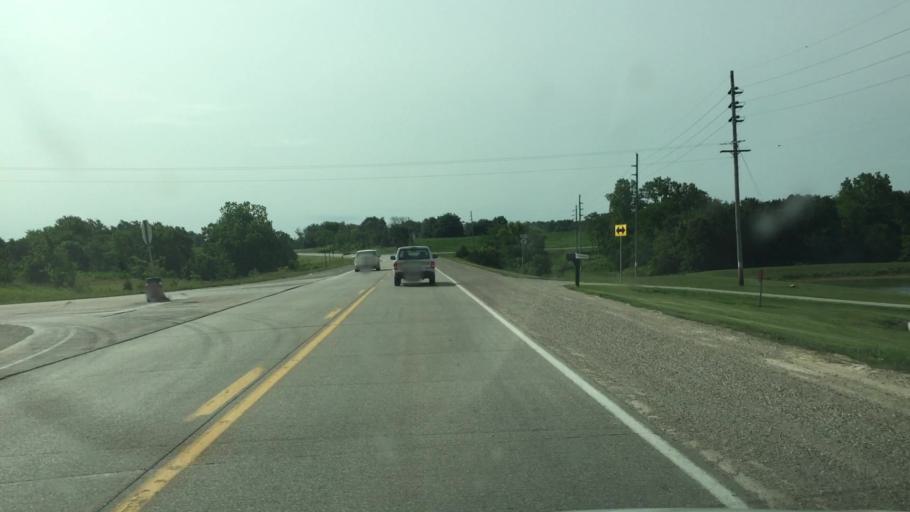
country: US
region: Illinois
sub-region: Hancock County
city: Nauvoo
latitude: 40.6354
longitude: -91.5175
